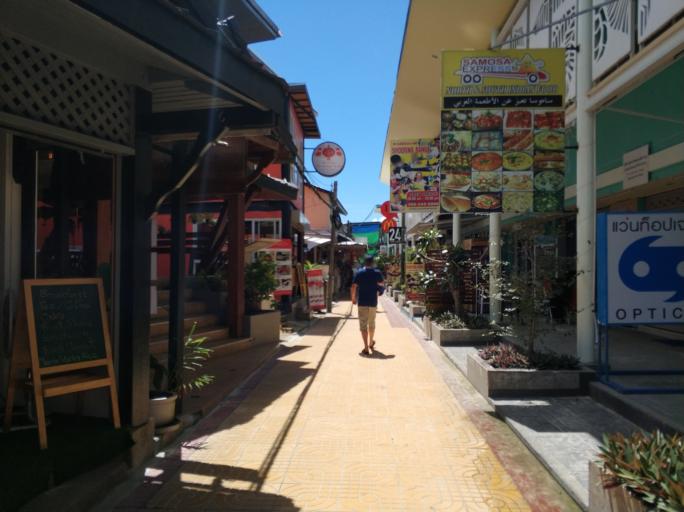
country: TH
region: Phangnga
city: Ban Phru Nai
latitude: 7.7393
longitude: 98.7709
